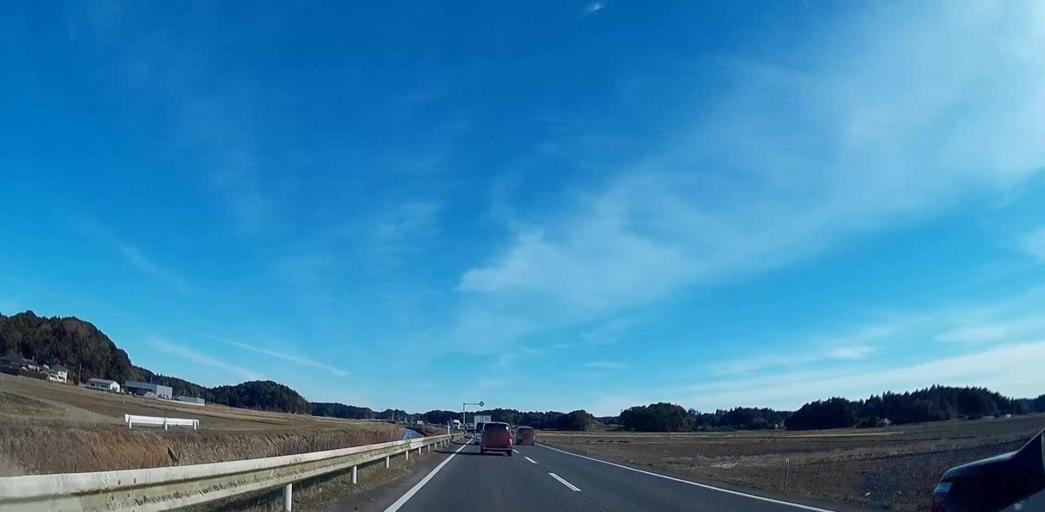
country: JP
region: Chiba
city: Yokaichiba
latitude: 35.7333
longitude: 140.5187
